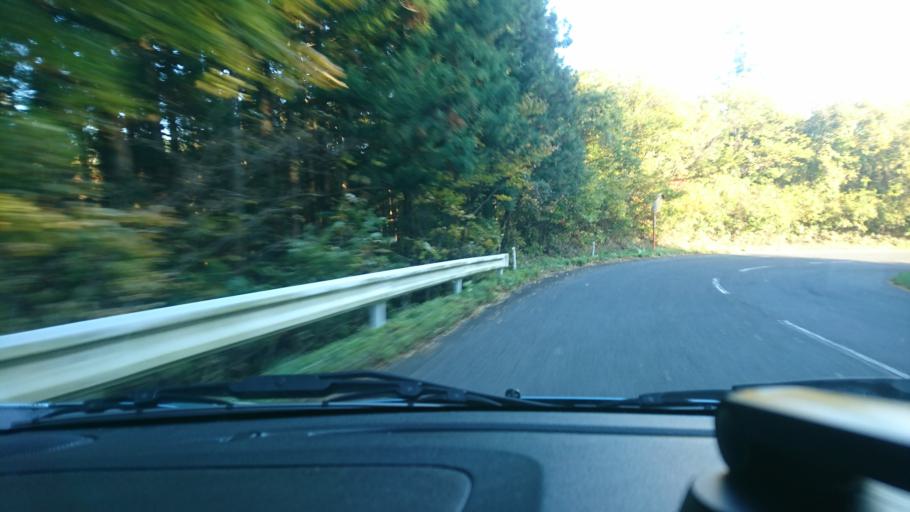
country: JP
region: Iwate
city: Ichinoseki
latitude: 38.7990
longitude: 141.2564
